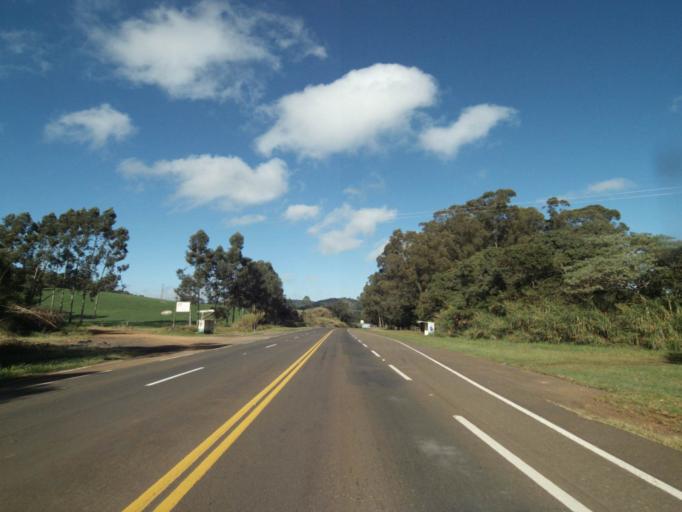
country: BR
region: Parana
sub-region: Faxinal
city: Faxinal
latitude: -23.8777
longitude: -51.1719
